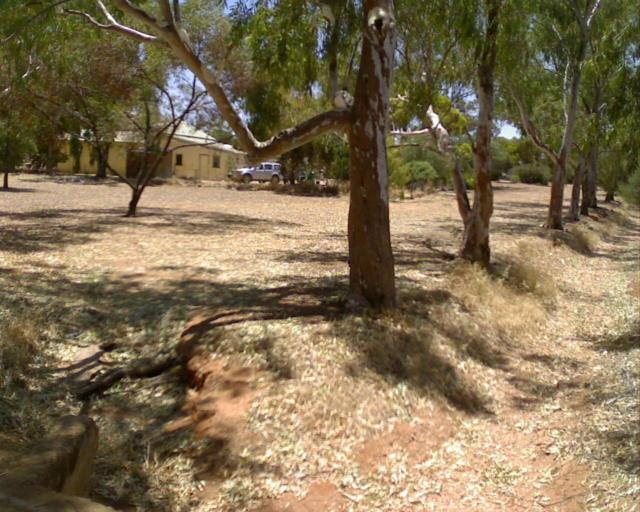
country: AU
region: Western Australia
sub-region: Wongan-Ballidu
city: Wongan Hills
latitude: -30.8282
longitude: 117.4805
